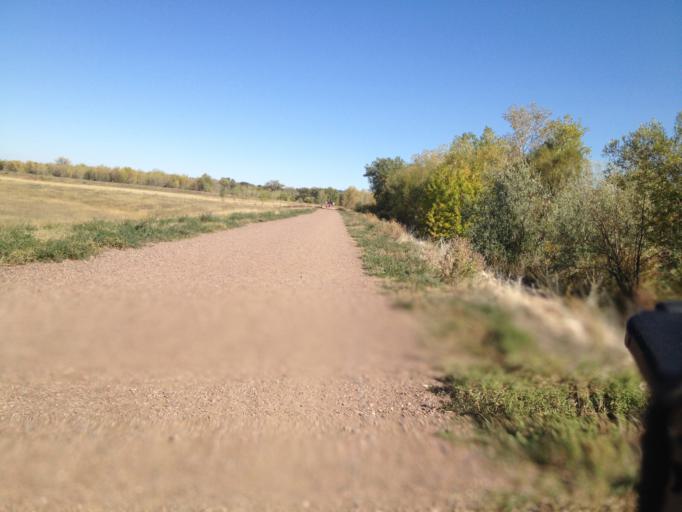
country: US
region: Colorado
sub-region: Boulder County
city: Boulder
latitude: 39.9717
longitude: -105.2328
